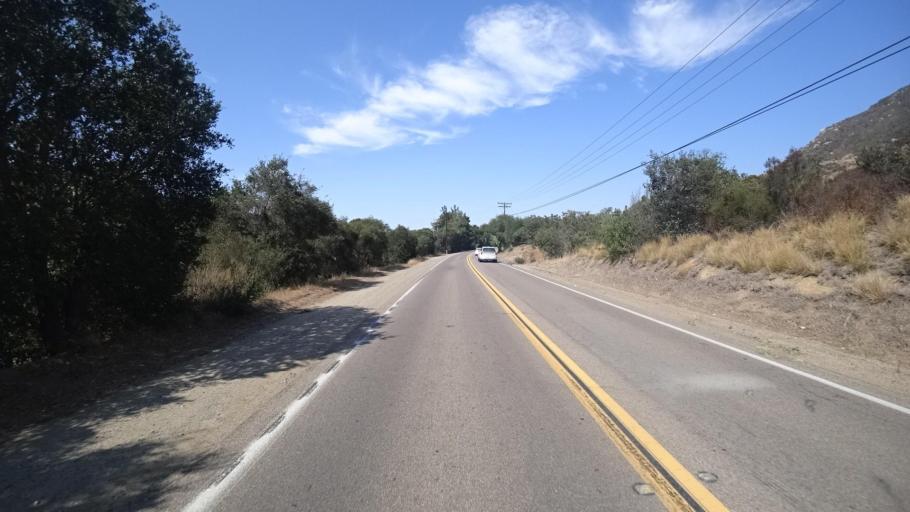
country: US
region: California
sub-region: San Diego County
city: Hidden Meadows
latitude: 33.1947
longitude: -117.1398
